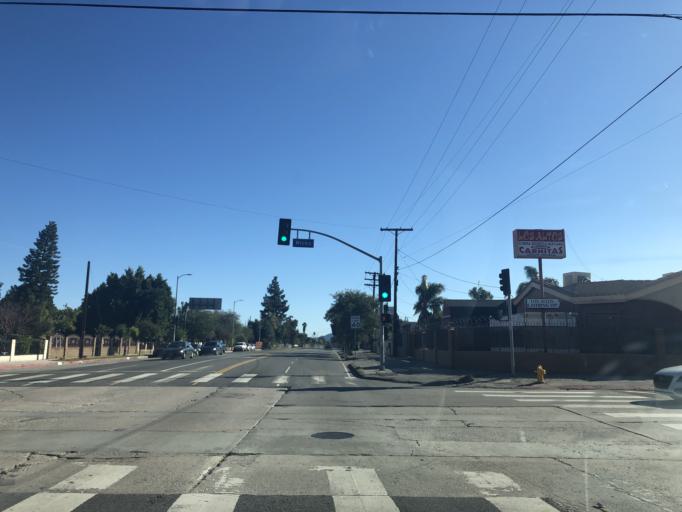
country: US
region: California
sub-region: Los Angeles County
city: North Hollywood
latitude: 34.2291
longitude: -118.4008
